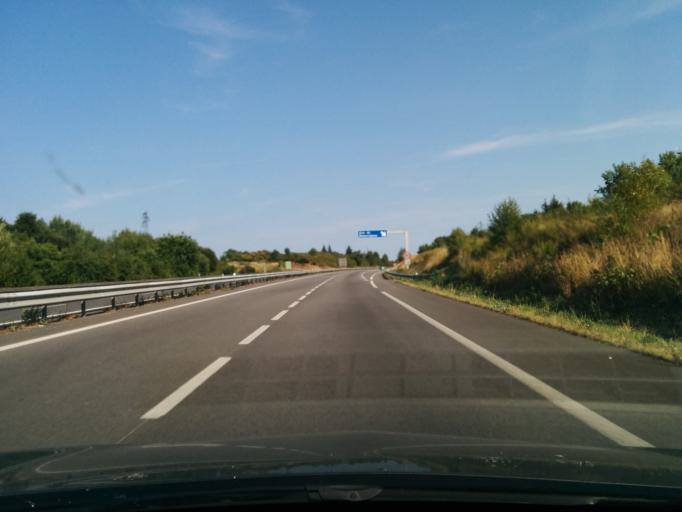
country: FR
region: Limousin
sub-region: Departement de la Haute-Vienne
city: Pierre-Buffiere
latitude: 45.6773
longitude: 1.3748
